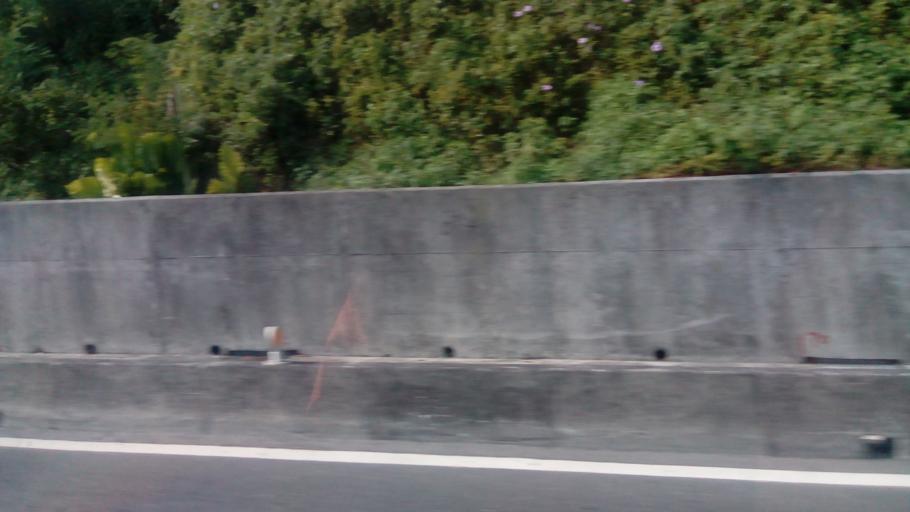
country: TW
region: Taiwan
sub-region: Yilan
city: Yilan
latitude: 24.5959
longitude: 121.8574
